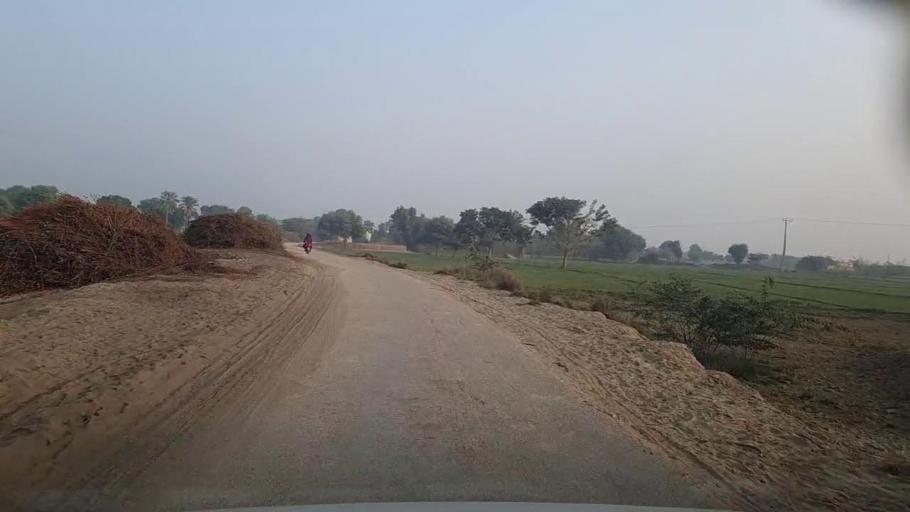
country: PK
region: Sindh
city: Bozdar
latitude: 27.0836
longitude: 68.5651
